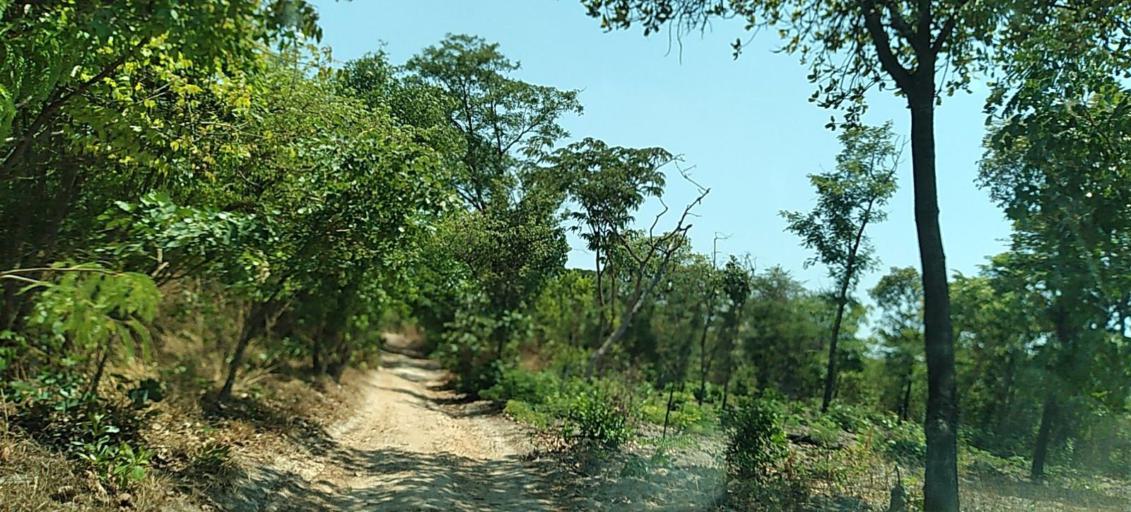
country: ZM
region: Copperbelt
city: Luanshya
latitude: -12.9820
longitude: 28.3296
